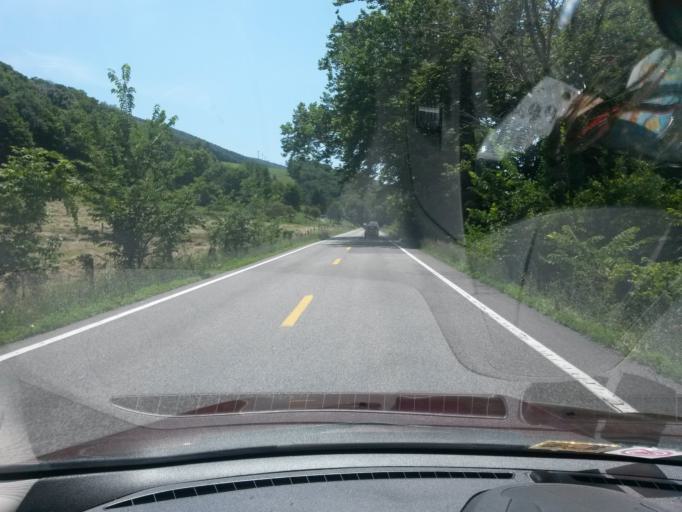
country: US
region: West Virginia
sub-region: Mineral County
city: Keyser
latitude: 39.3262
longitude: -79.0759
